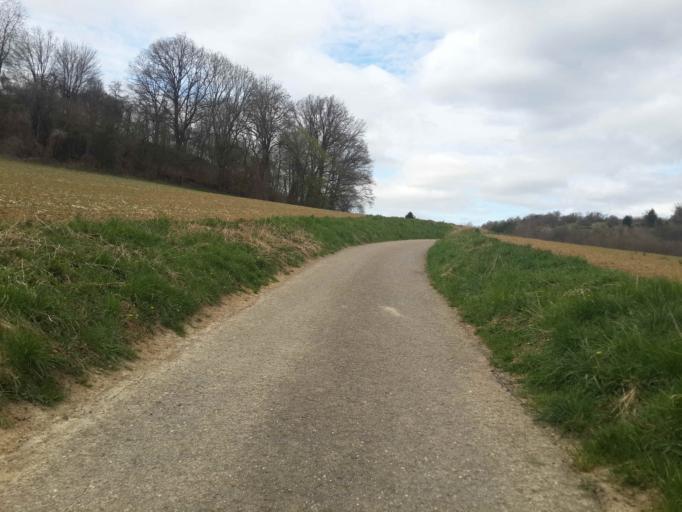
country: DE
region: Baden-Wuerttemberg
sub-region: Karlsruhe Region
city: Billigheim
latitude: 49.3156
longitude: 9.2441
